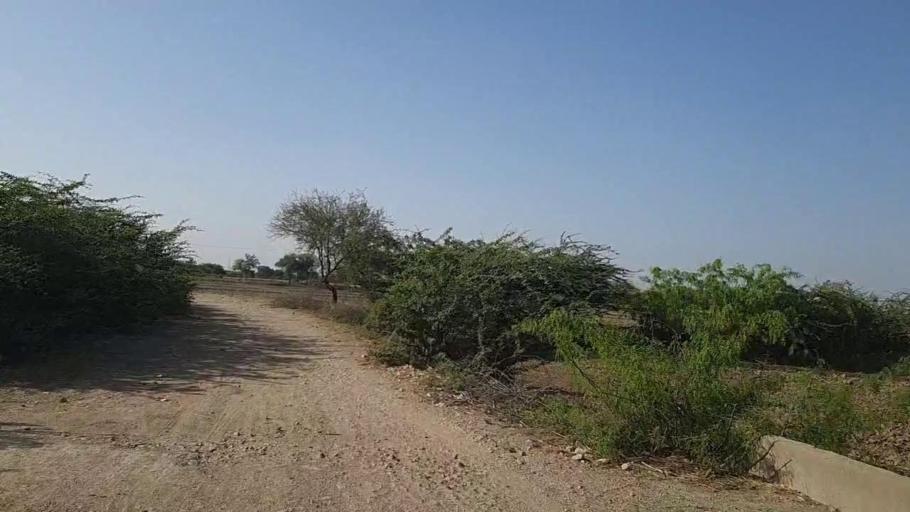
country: PK
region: Sindh
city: Kotri
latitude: 25.1409
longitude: 68.2792
